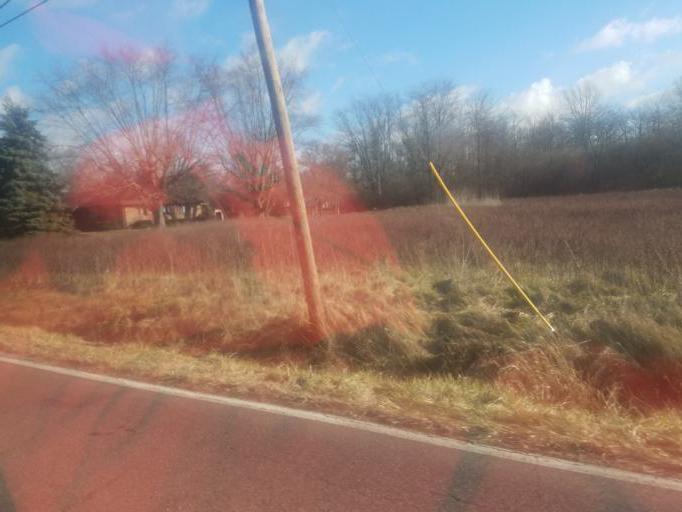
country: US
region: Ohio
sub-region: Marion County
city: Marion
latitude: 40.5635
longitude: -83.1598
